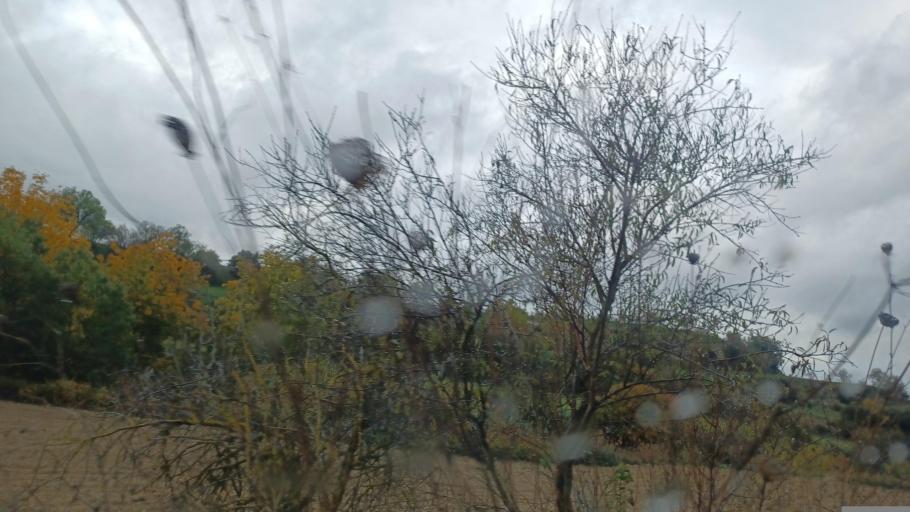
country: CY
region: Pafos
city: Mesogi
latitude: 34.8600
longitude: 32.5415
